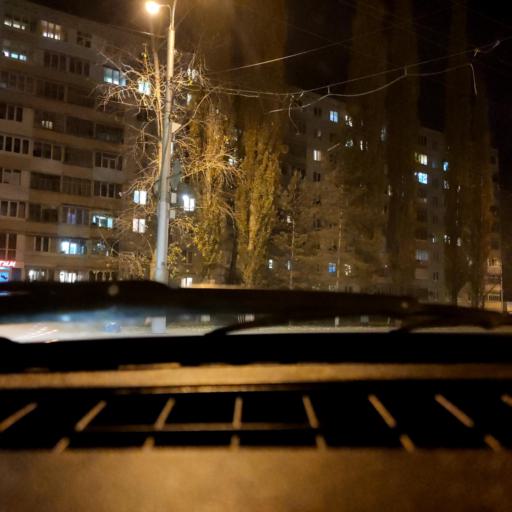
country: RU
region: Bashkortostan
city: Ufa
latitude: 54.7834
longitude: 56.1243
